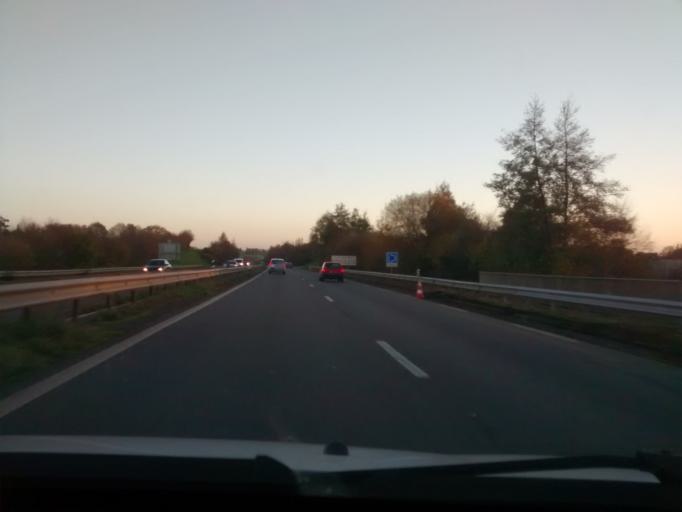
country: FR
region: Brittany
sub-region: Departement d'Ille-et-Vilaine
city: Vignoc
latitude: 48.2592
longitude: -1.7766
